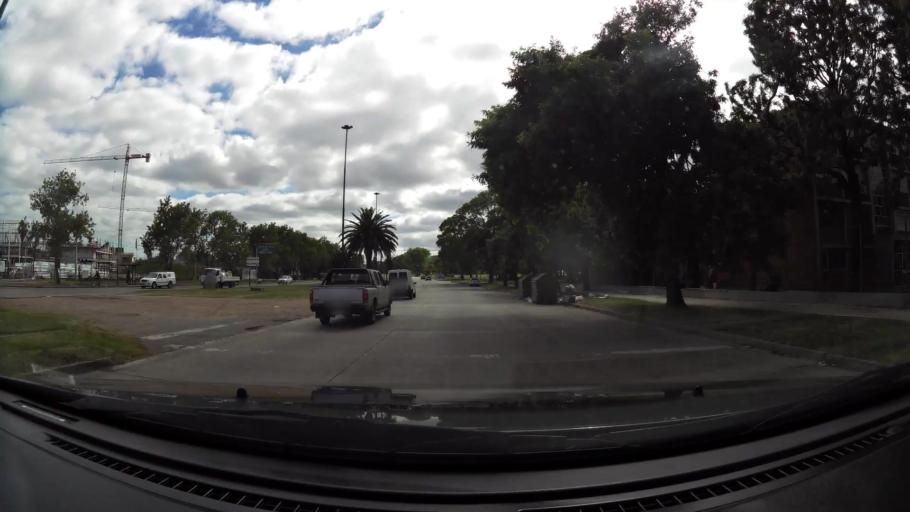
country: UY
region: Montevideo
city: Montevideo
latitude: -34.8650
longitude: -56.1538
